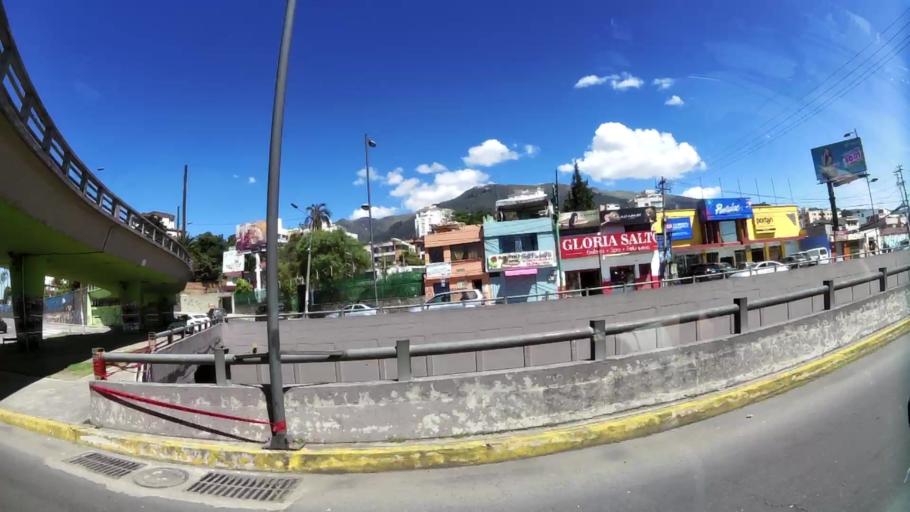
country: EC
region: Pichincha
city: Quito
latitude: -0.1661
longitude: -78.4869
